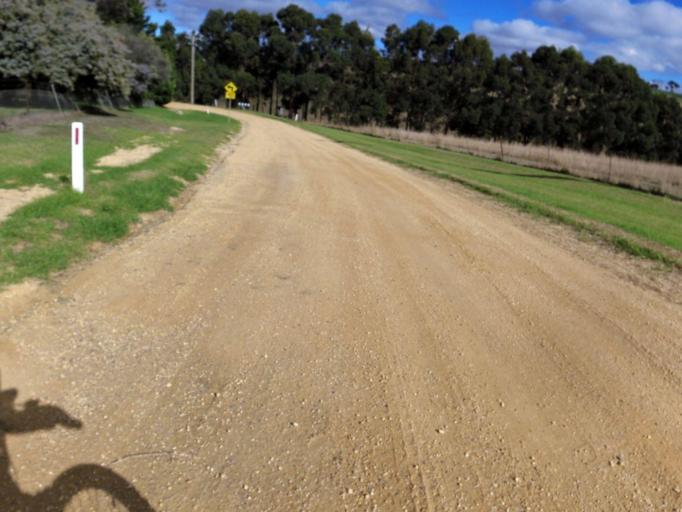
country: AU
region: Victoria
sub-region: Greater Geelong
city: Wandana Heights
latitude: -38.1840
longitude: 144.2975
